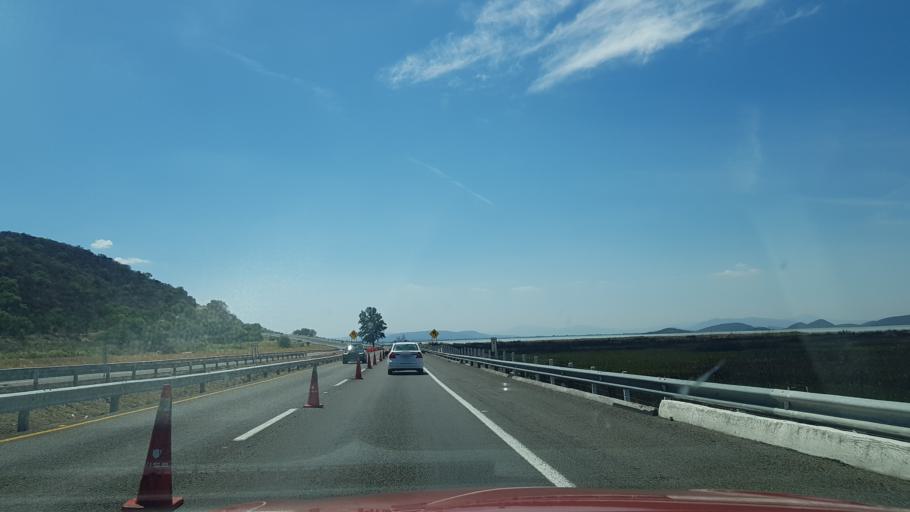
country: MX
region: Michoacan
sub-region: Zinapecuaro
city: Jose Maria Morelos (La Yegueeria)
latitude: 19.8982
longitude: -100.8903
